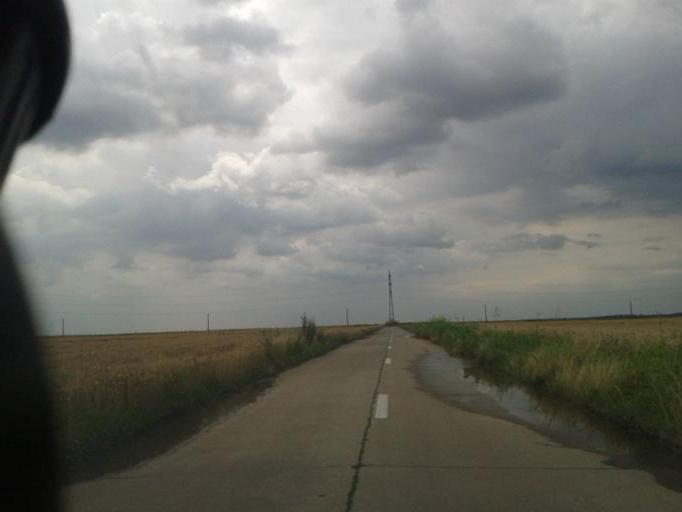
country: RO
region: Calarasi
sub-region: Comuna Belciugatele
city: Belciugatele
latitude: 44.5412
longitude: 26.4636
